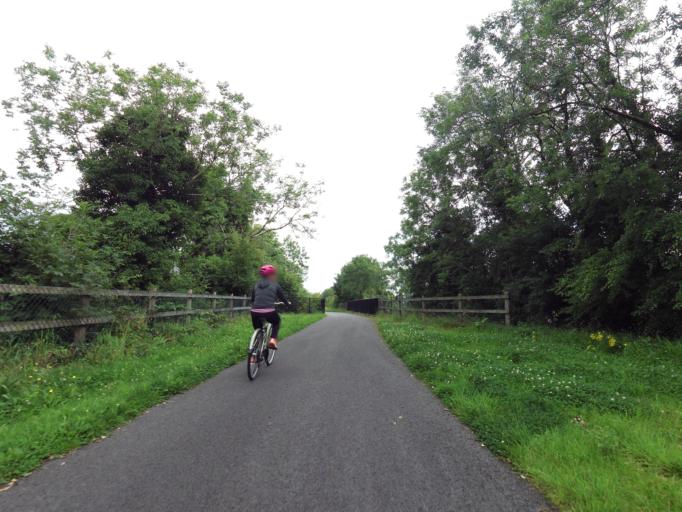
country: IE
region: Leinster
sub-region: An Iarmhi
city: An Muileann gCearr
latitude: 53.5098
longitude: -7.3865
